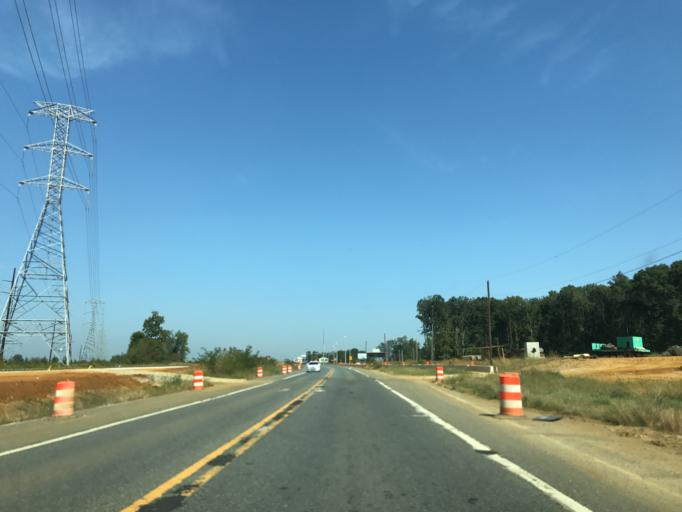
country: US
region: Delaware
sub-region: New Castle County
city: Middletown
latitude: 39.4156
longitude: -75.7662
